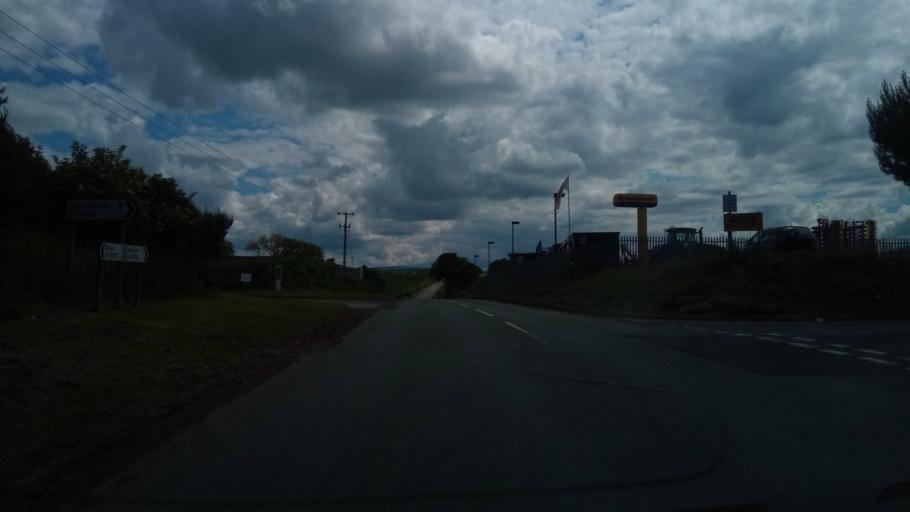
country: GB
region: Scotland
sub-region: The Scottish Borders
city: Kelso
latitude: 55.5854
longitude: -2.4219
